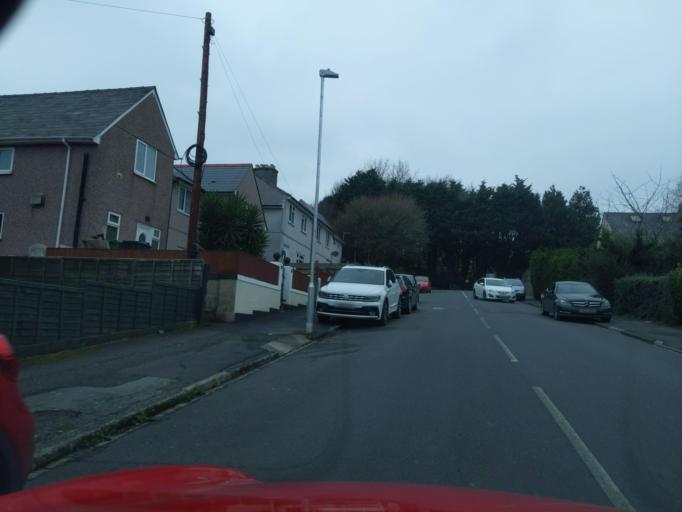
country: GB
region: England
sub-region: Plymouth
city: Plymstock
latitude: 50.3768
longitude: -4.1121
